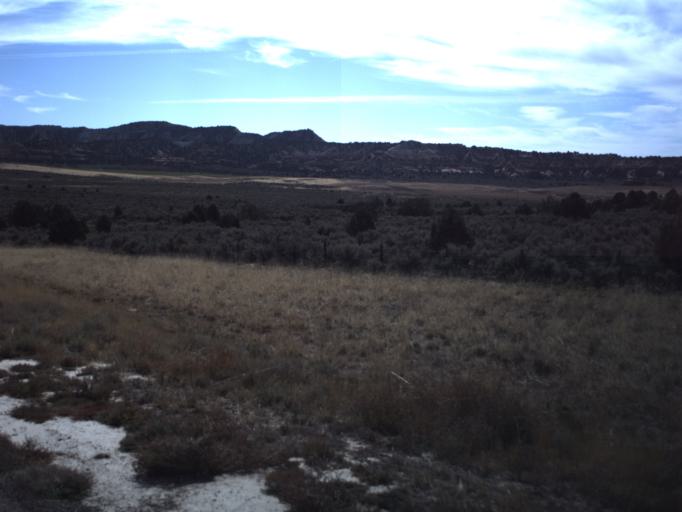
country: US
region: Utah
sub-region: Garfield County
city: Panguitch
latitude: 37.5632
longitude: -112.0347
